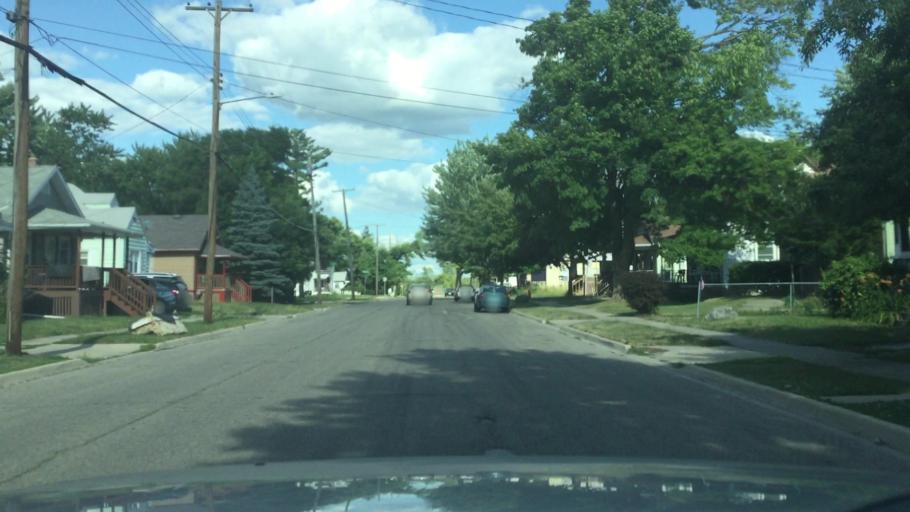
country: US
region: Michigan
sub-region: Saginaw County
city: Saginaw
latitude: 43.4006
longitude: -83.9816
